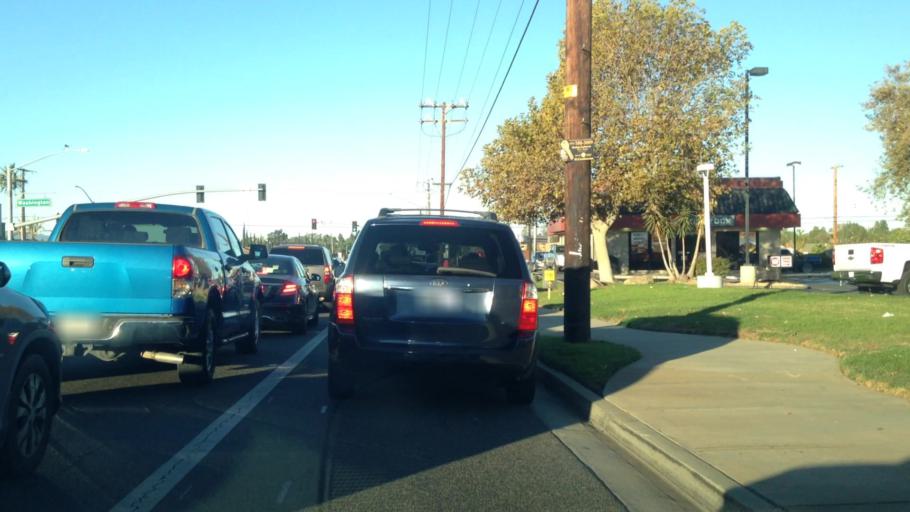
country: US
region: California
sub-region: Riverside County
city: Woodcrest
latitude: 33.8825
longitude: -117.3651
